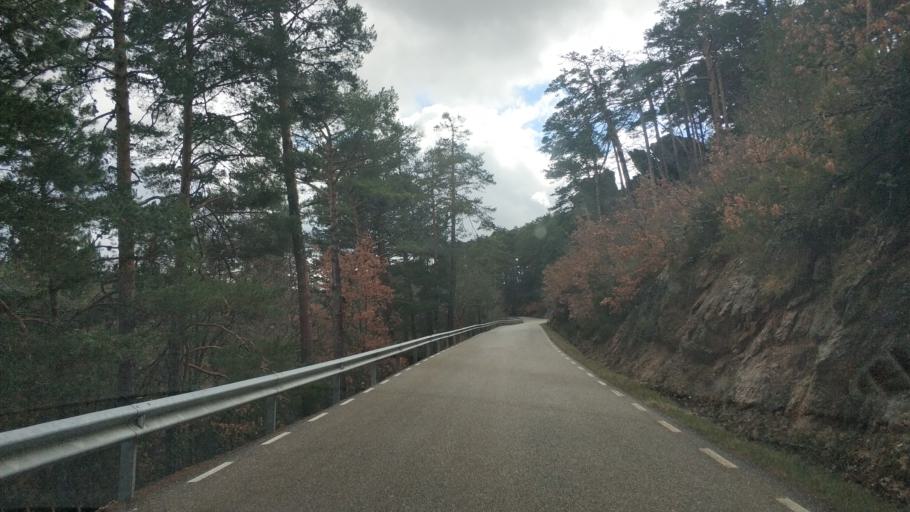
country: ES
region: Castille and Leon
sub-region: Provincia de Burgos
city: Quintanar de la Sierra
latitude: 42.0019
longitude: -3.0178
